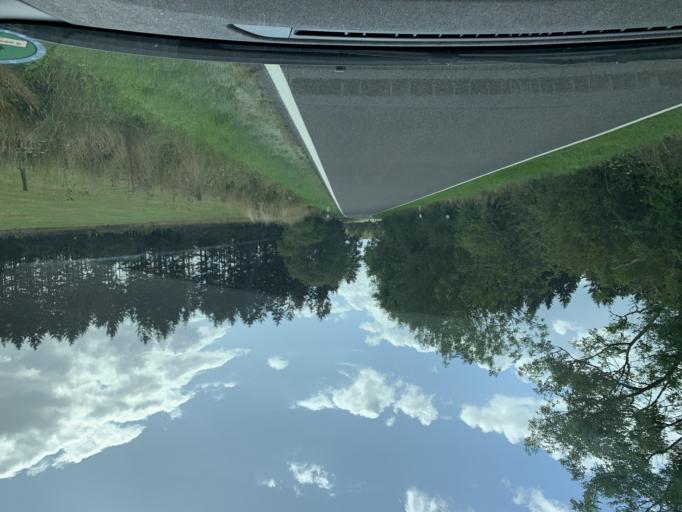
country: DE
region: North Rhine-Westphalia
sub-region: Regierungsbezirk Koln
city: Simmerath
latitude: 50.6156
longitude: 6.2718
